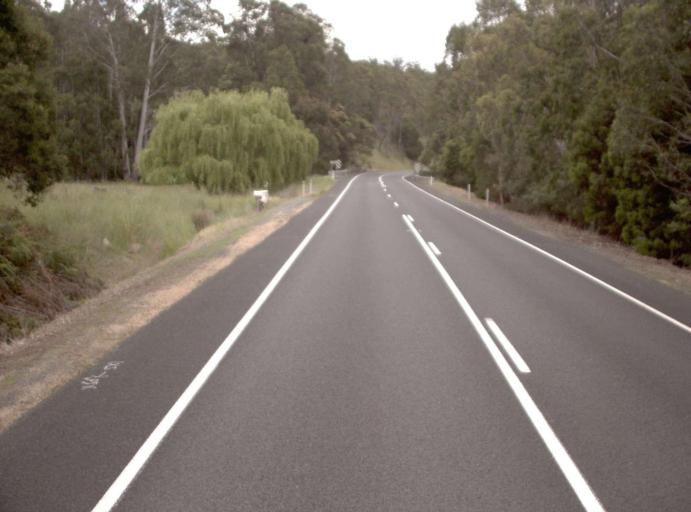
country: AU
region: New South Wales
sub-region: Bombala
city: Bombala
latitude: -37.3335
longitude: 149.2061
